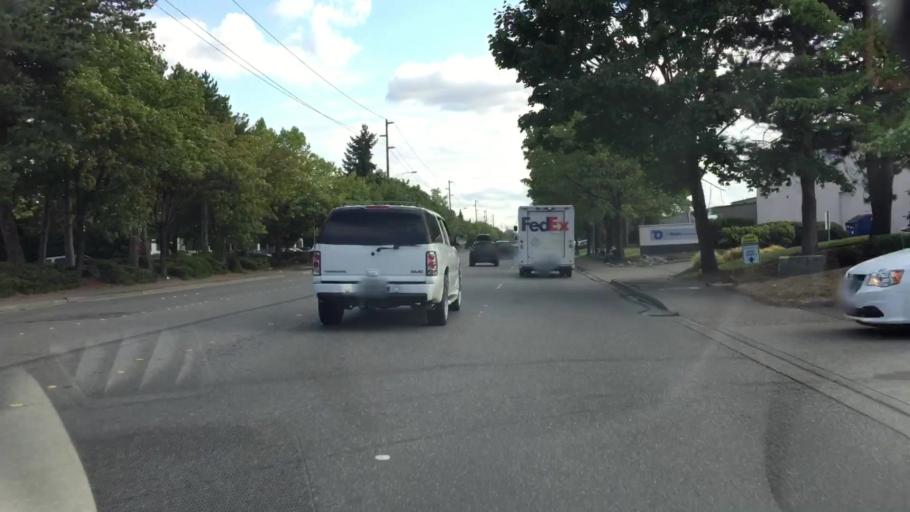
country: US
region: Washington
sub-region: King County
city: Kent
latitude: 47.4194
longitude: -122.2281
